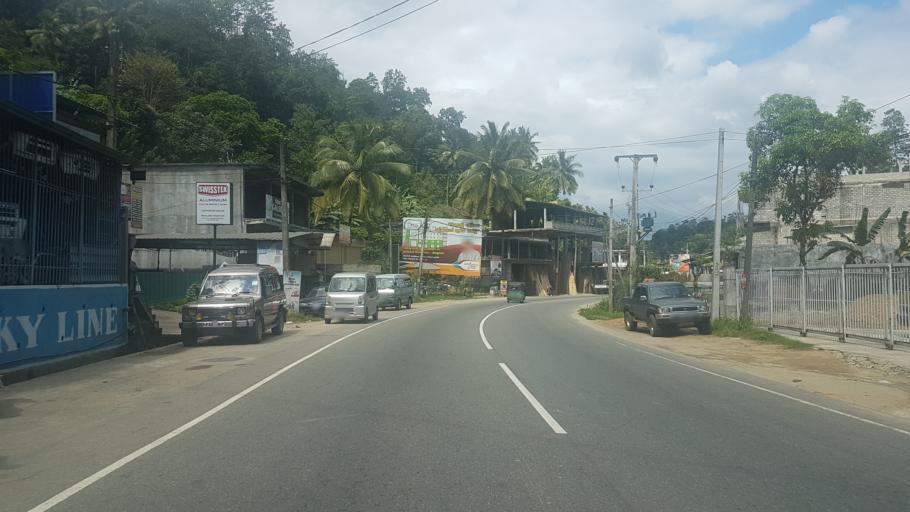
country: LK
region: Central
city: Gampola
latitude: 7.2105
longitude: 80.5985
